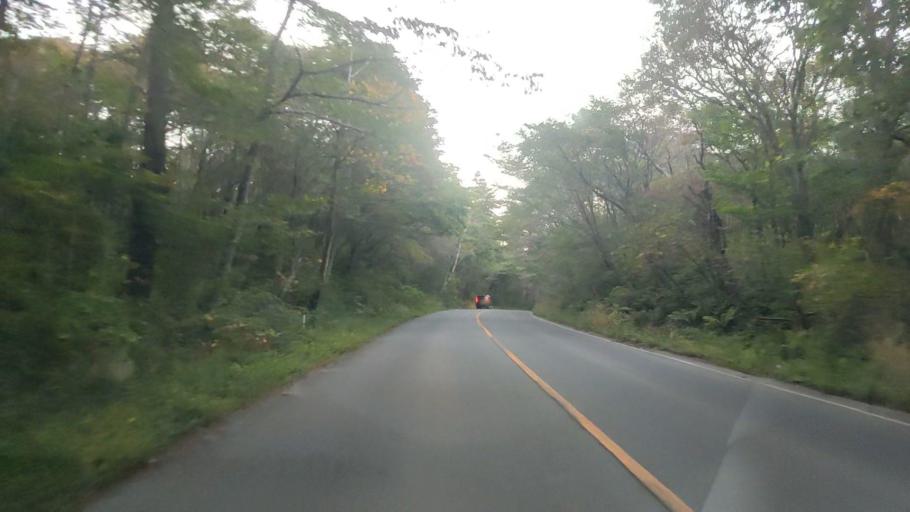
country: JP
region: Nagano
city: Komoro
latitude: 36.4166
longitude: 138.5702
